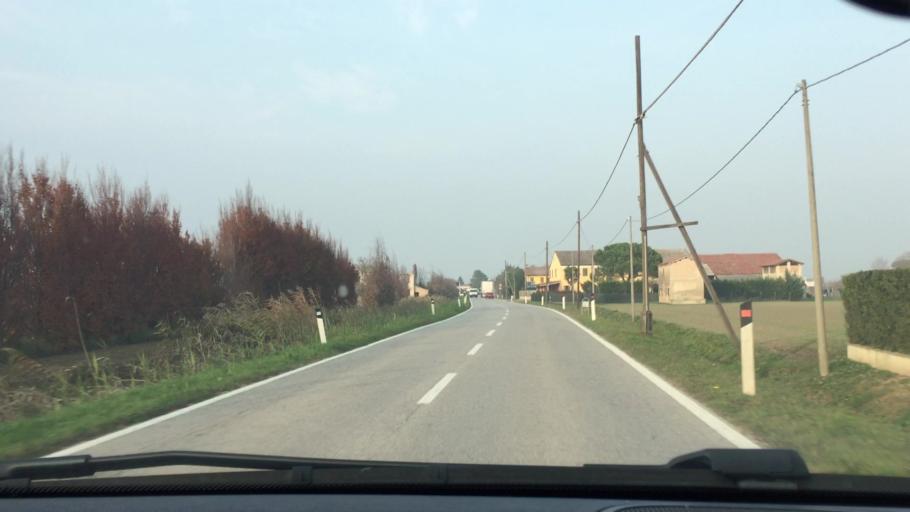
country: IT
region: Veneto
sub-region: Provincia di Padova
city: Bovolenta
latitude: 45.2812
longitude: 11.9416
